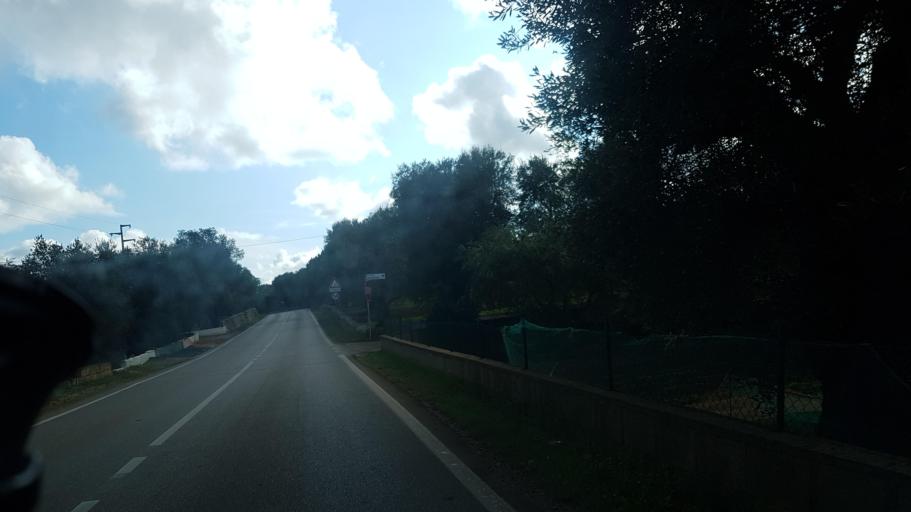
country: IT
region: Apulia
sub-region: Provincia di Brindisi
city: San Michele Salentino
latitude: 40.6593
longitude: 17.6010
